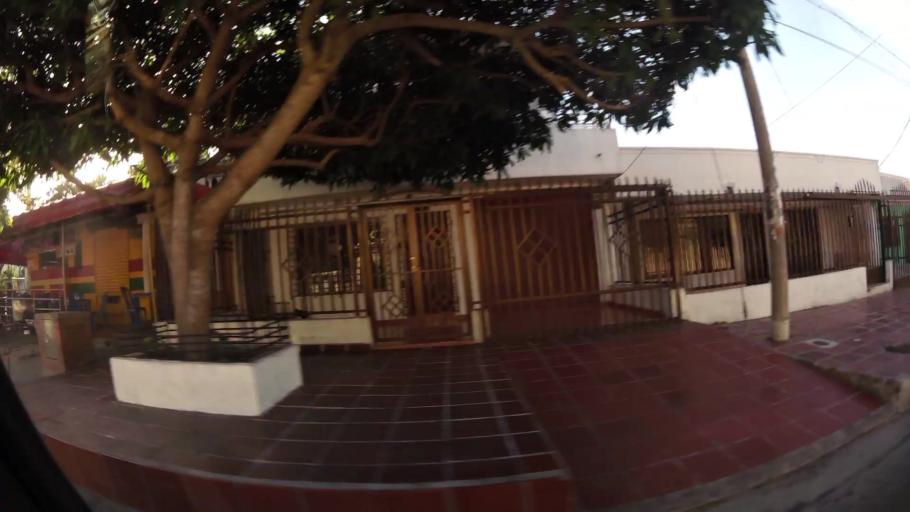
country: CO
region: Atlantico
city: Barranquilla
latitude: 10.9847
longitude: -74.8081
